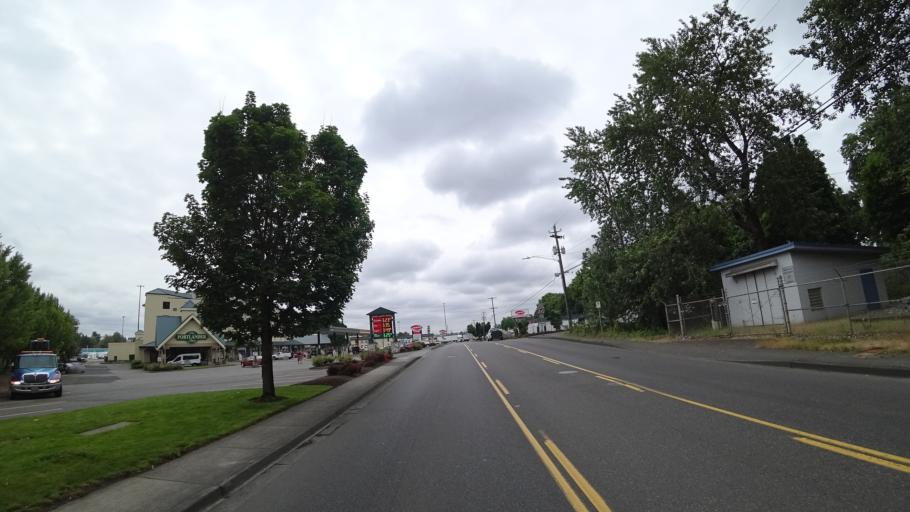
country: US
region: Washington
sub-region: Clark County
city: Vancouver
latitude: 45.5978
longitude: -122.6711
